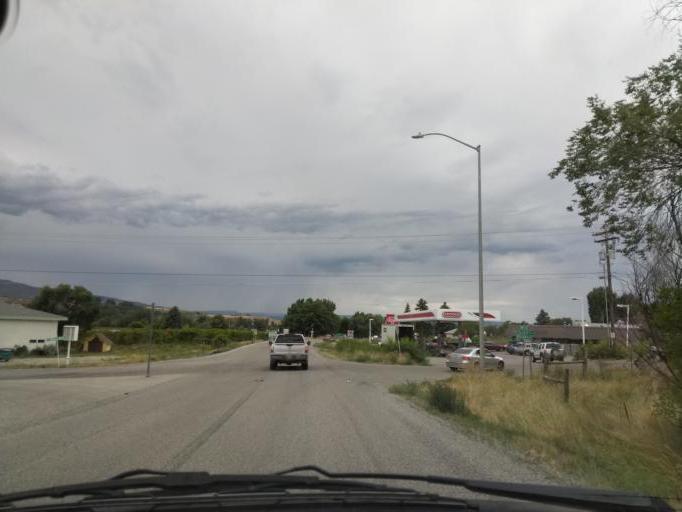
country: US
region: Colorado
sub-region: Delta County
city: Paonia
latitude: 38.8720
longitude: -107.6102
